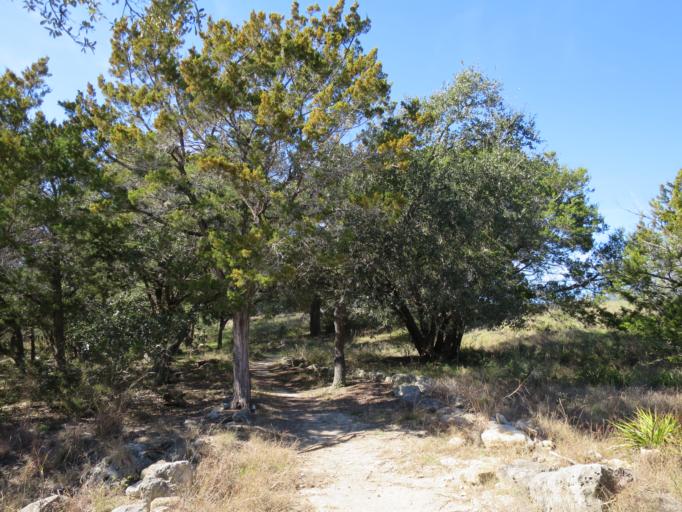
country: US
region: Texas
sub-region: Travis County
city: Lakeway
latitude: 30.3803
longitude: -97.9670
